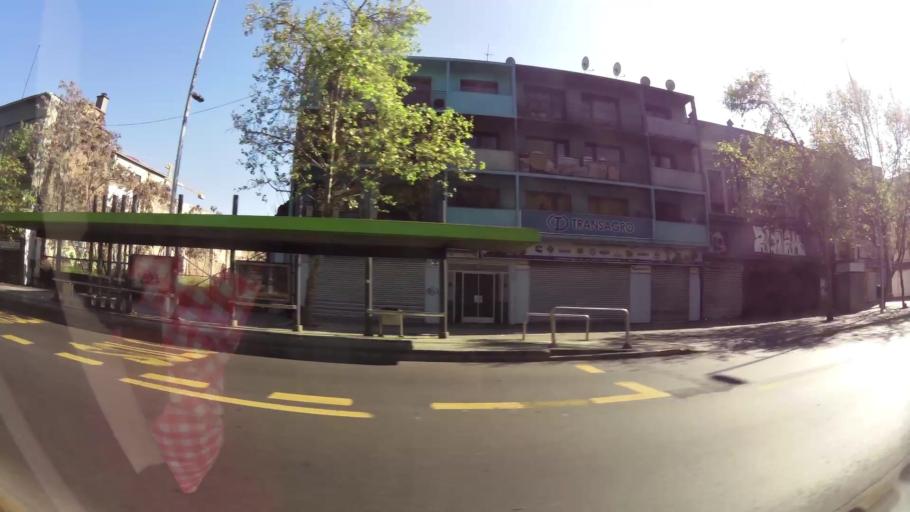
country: CL
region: Santiago Metropolitan
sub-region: Provincia de Santiago
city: Santiago
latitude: -33.4465
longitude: -70.6633
